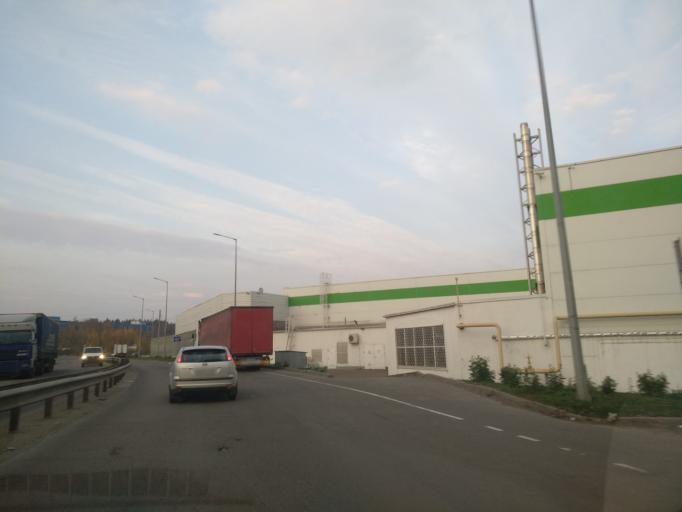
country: RU
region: Moscow
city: Lianozovo
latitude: 55.9150
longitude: 37.5713
